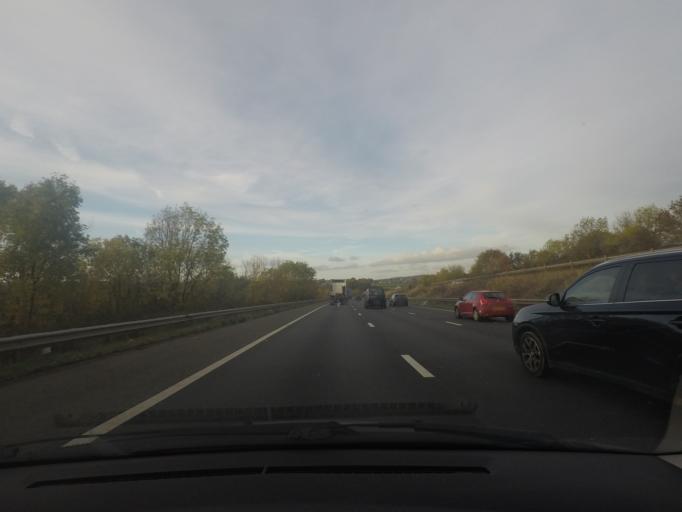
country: GB
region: England
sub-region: Barnsley
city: Darton
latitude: 53.5691
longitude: -1.5412
